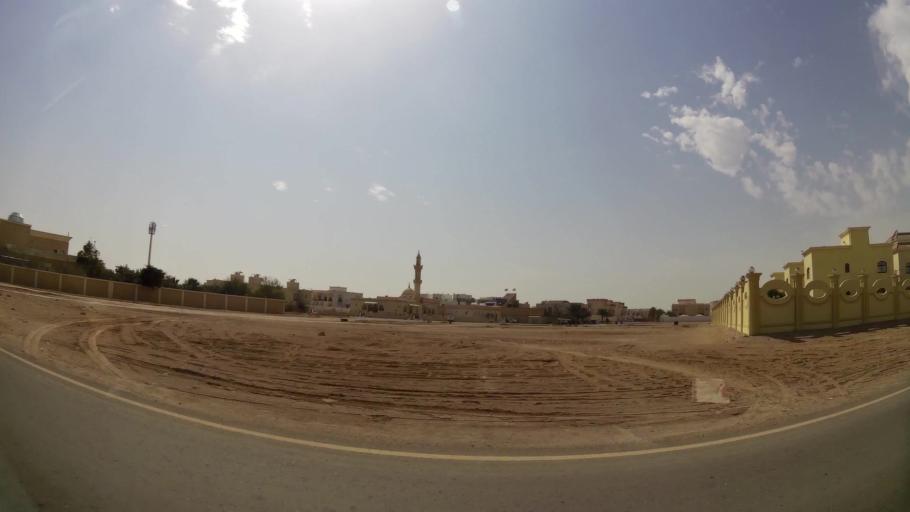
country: AE
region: Abu Dhabi
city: Abu Dhabi
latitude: 24.3383
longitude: 54.5646
